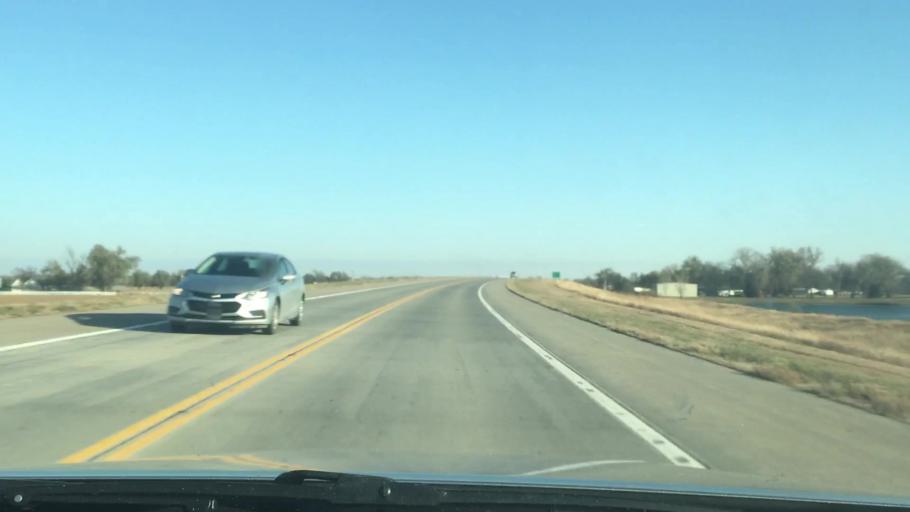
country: US
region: Kansas
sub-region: Reno County
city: Nickerson
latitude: 38.1041
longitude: -98.0187
